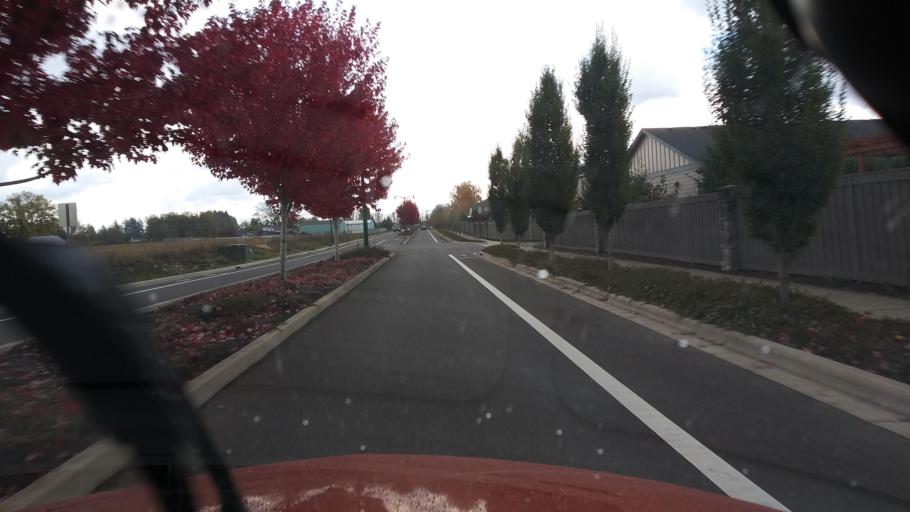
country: US
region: Oregon
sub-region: Washington County
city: Forest Grove
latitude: 45.5391
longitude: -123.1123
